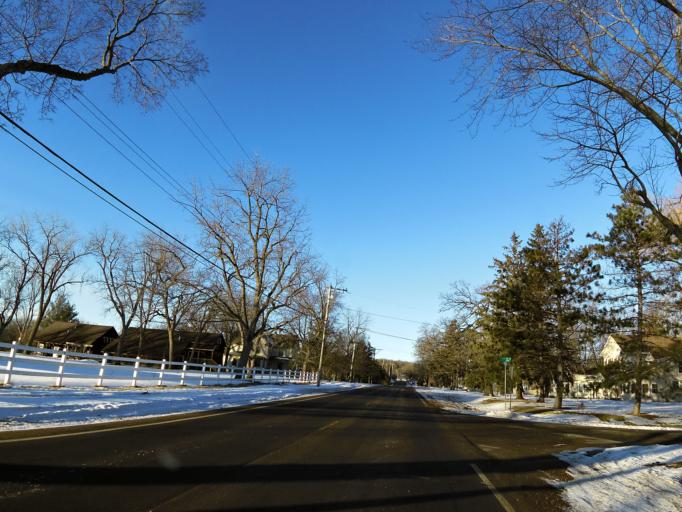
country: US
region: Minnesota
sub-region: Washington County
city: Cottage Grove
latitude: 44.8432
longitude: -92.8814
